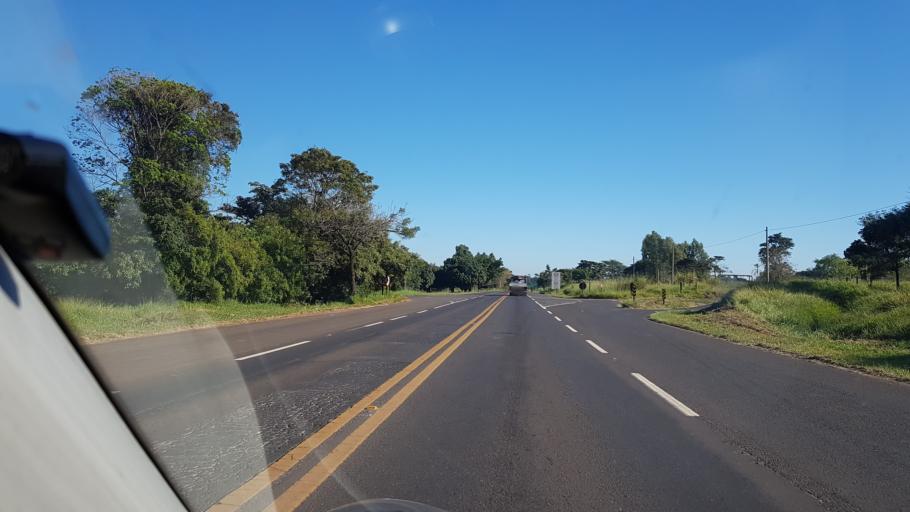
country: BR
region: Sao Paulo
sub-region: Assis
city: Assis
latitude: -22.6326
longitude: -50.4380
